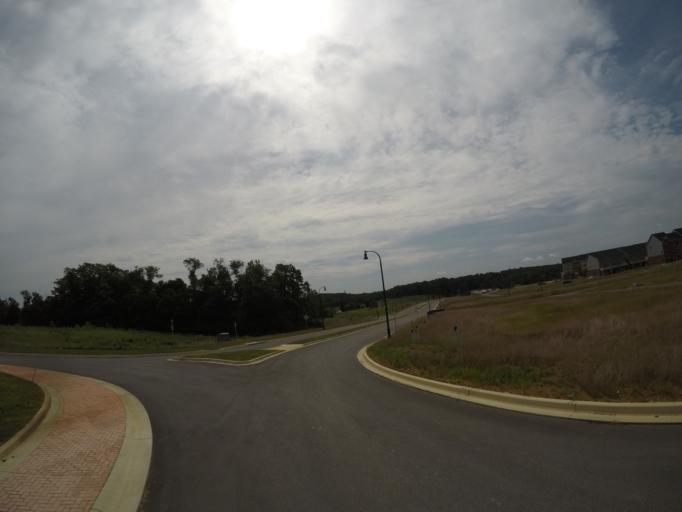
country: US
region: Maryland
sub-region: Montgomery County
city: Clarksburg
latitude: 39.2201
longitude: -77.2844
